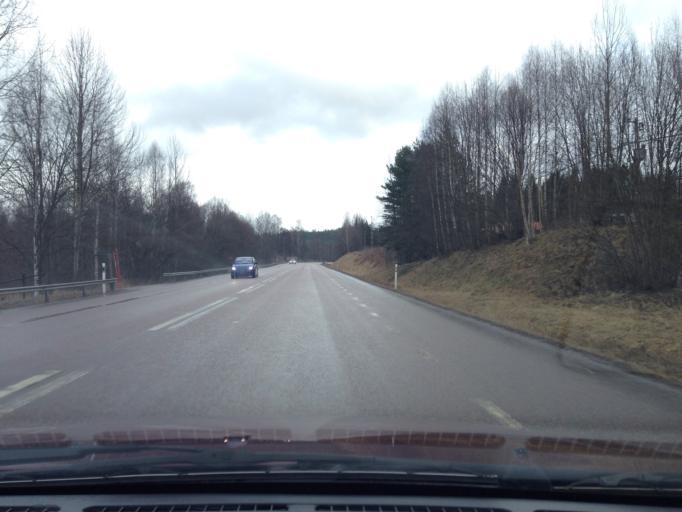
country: SE
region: Dalarna
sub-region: Ludvika Kommun
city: Ludvika
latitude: 60.1546
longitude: 15.2320
